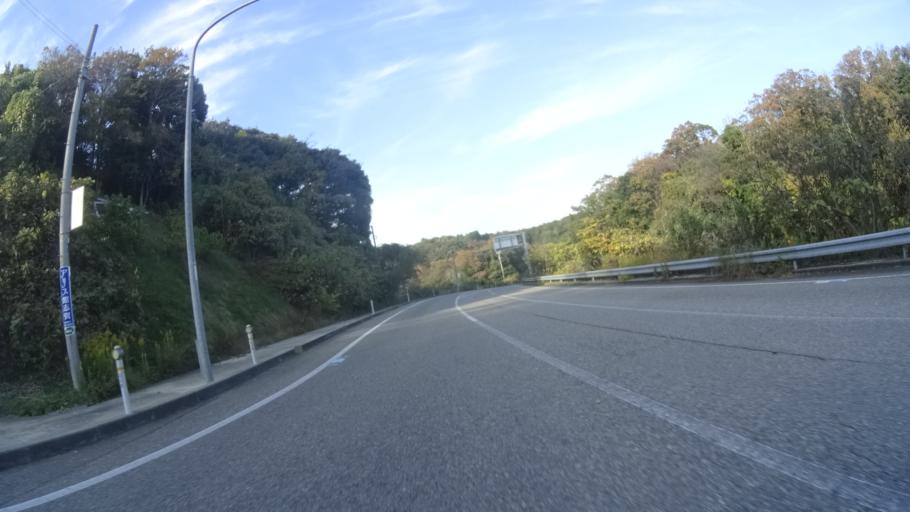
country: JP
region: Ishikawa
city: Hakui
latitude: 37.0778
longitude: 136.7293
